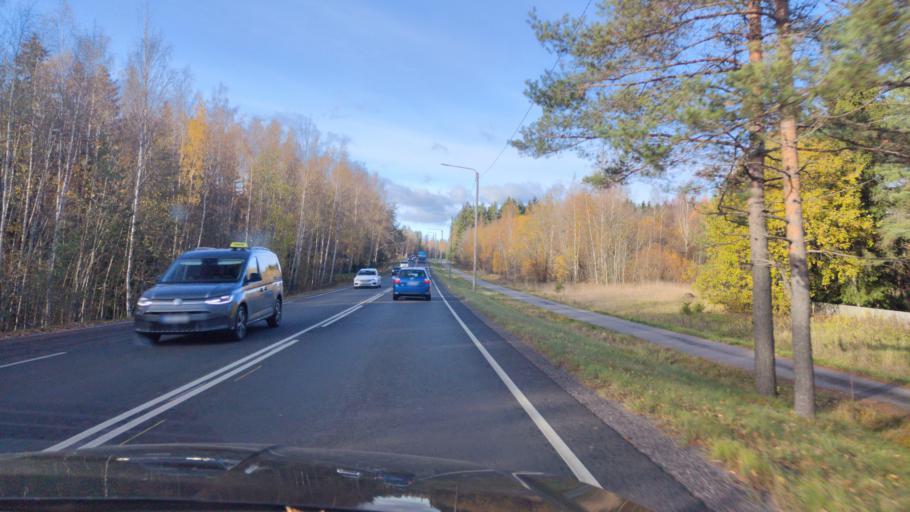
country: FI
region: Varsinais-Suomi
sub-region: Turku
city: Kaarina
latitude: 60.4528
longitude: 22.3708
